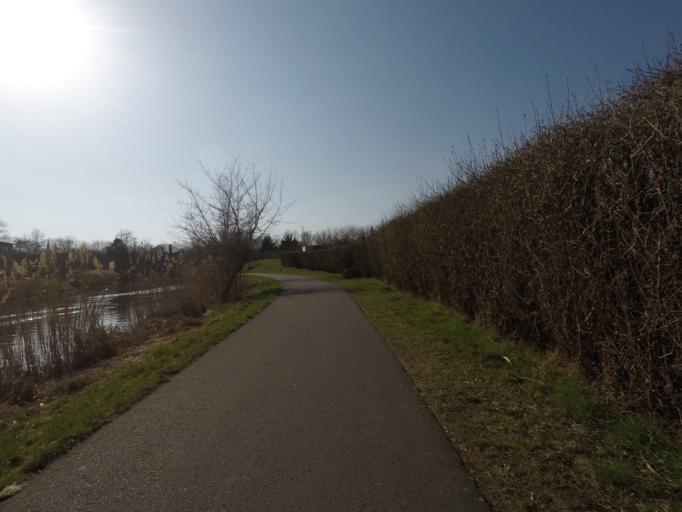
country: DE
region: Brandenburg
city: Eberswalde
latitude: 52.8390
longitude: 13.8039
